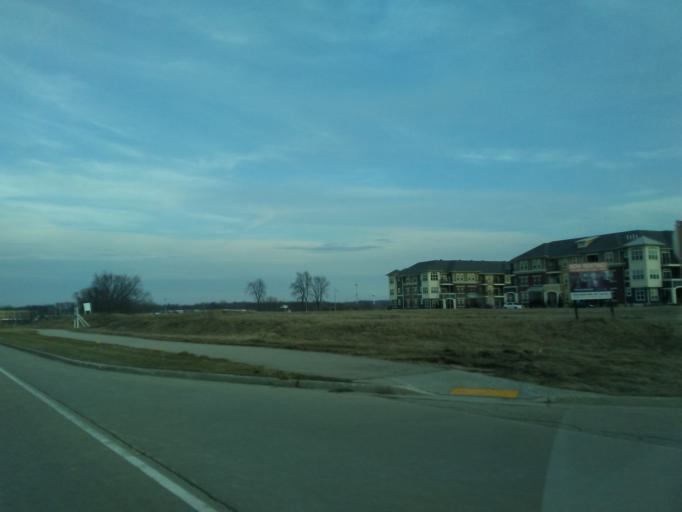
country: US
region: Wisconsin
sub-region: Dane County
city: Verona
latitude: 42.9876
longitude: -89.5556
